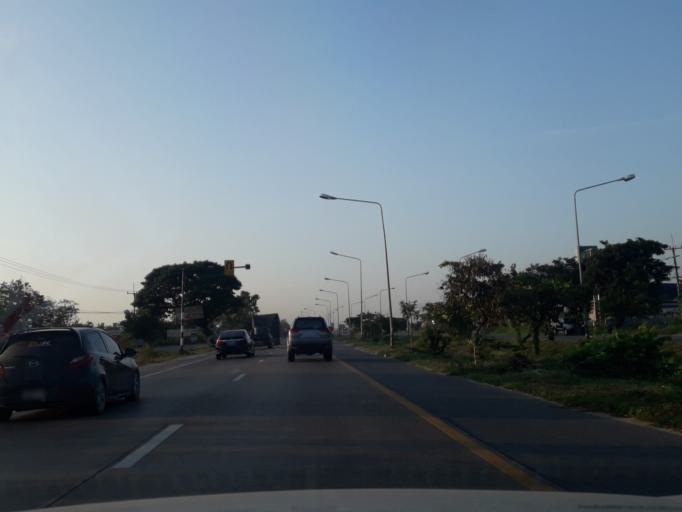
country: TH
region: Phra Nakhon Si Ayutthaya
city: Phra Nakhon Si Ayutthaya
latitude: 14.3417
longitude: 100.5282
